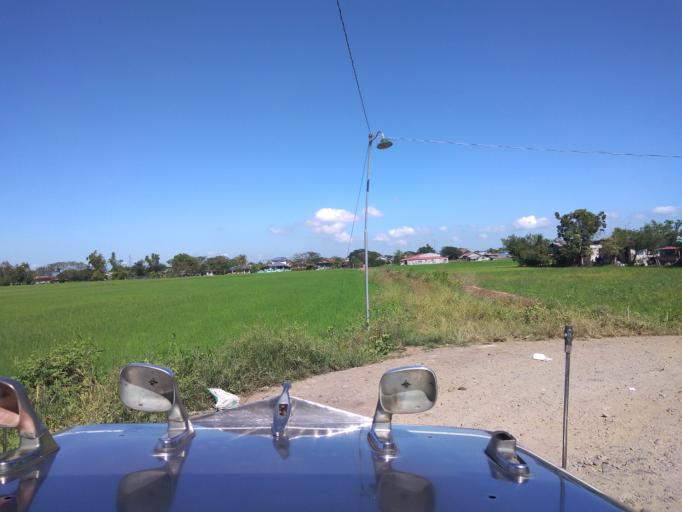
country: PH
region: Central Luzon
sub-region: Province of Pampanga
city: Batasan Bata
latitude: 15.1615
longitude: 120.9186
